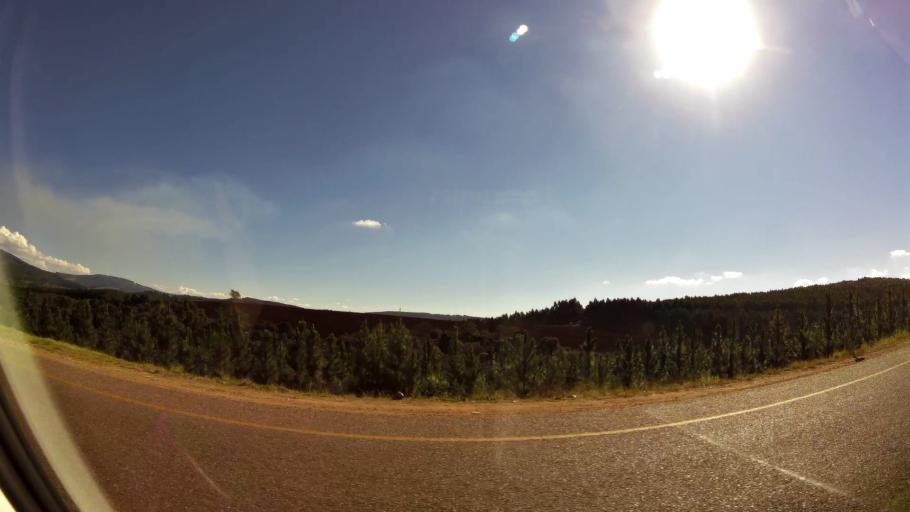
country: ZA
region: Limpopo
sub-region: Capricorn District Municipality
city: Mankoeng
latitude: -23.9312
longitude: 29.9567
